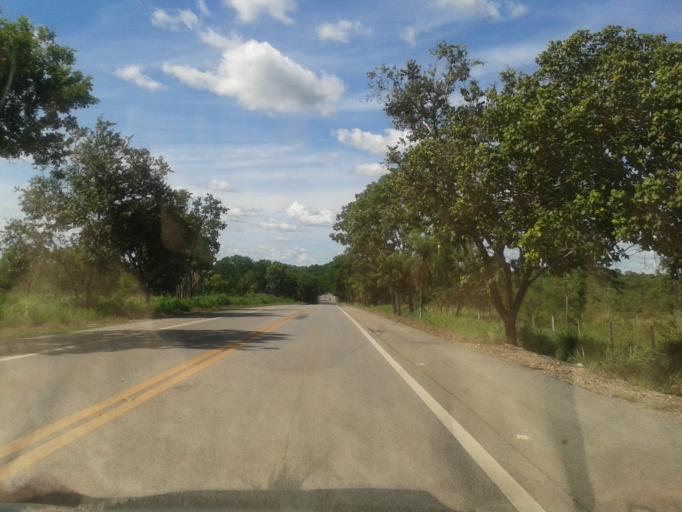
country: BR
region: Goias
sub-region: Itapuranga
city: Itapuranga
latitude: -15.4122
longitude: -50.3779
